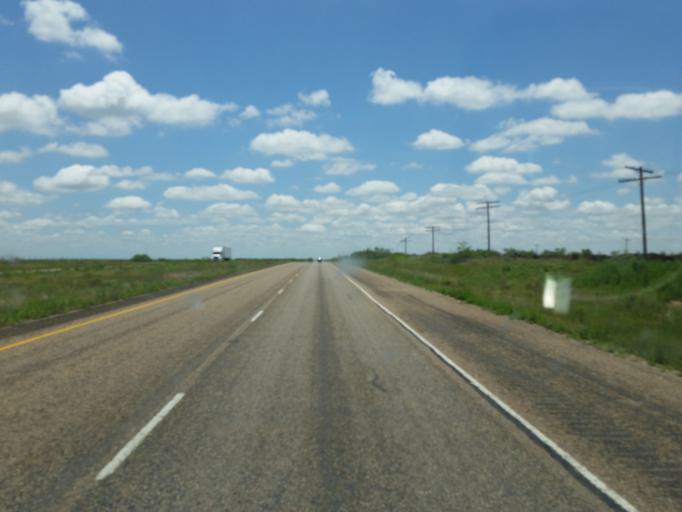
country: US
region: Texas
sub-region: Garza County
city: Post
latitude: 33.1309
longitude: -101.3005
